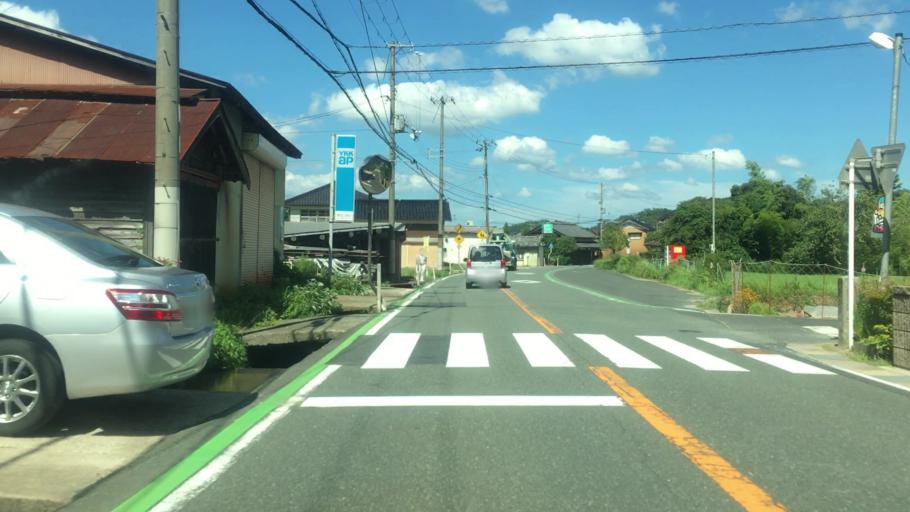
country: JP
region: Kyoto
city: Miyazu
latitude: 35.5869
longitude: 135.0364
